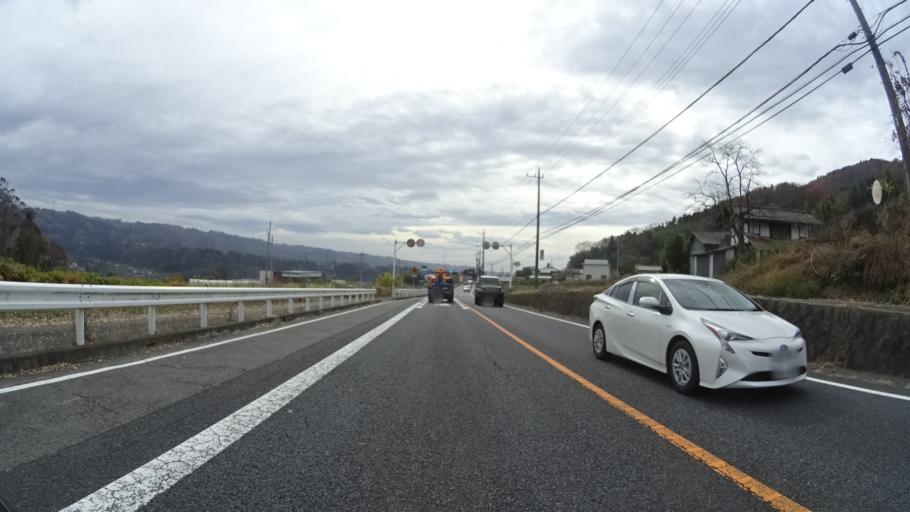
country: JP
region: Gunma
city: Numata
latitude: 36.5619
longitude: 139.0378
